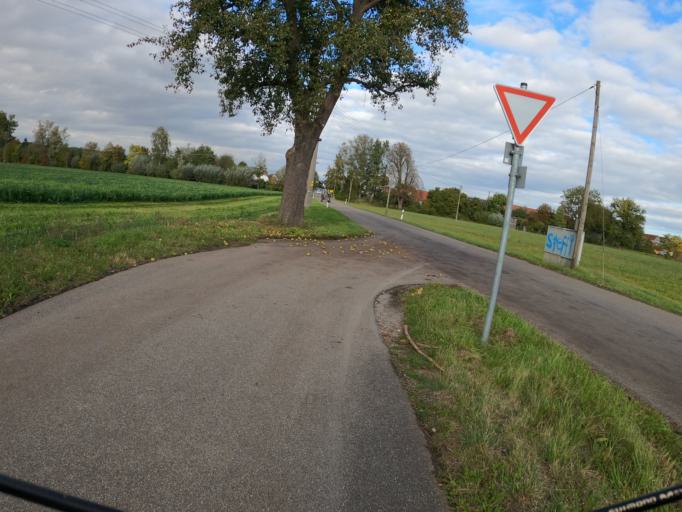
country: DE
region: Bavaria
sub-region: Swabia
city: Holzheim
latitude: 48.3981
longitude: 10.1003
